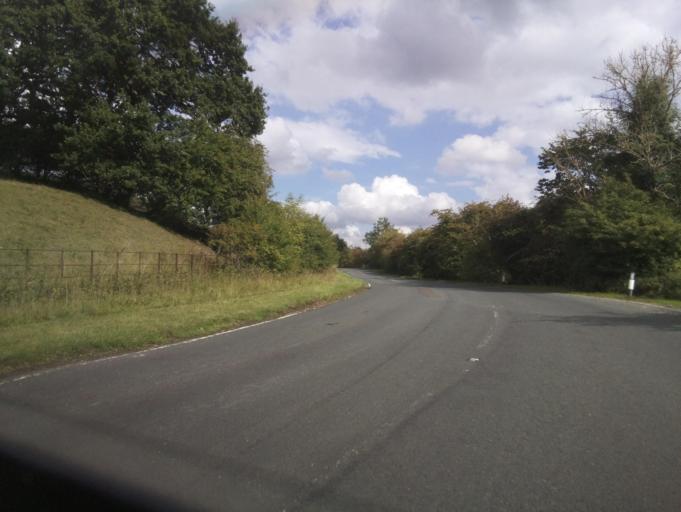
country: GB
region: England
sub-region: North Yorkshire
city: Catterick Garrison
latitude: 54.4018
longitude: -1.7683
